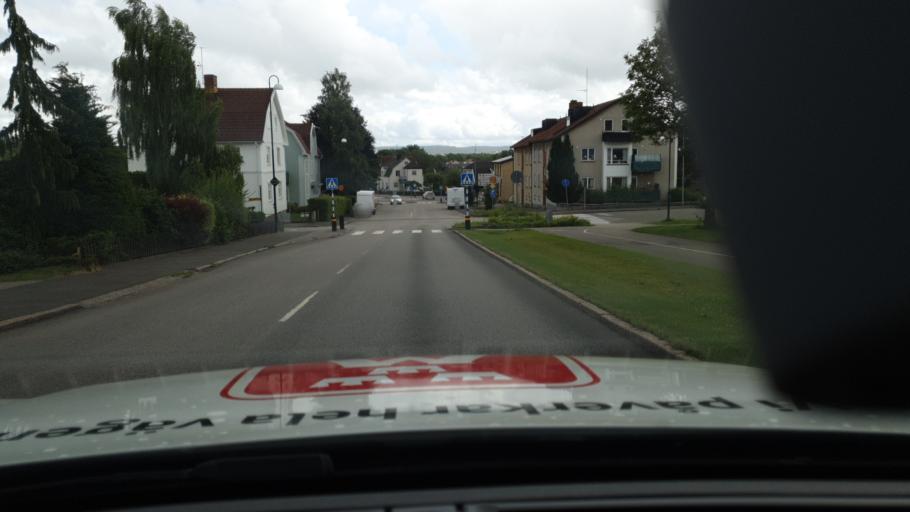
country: SE
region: Vaestra Goetaland
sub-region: Falkopings Kommun
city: Falkoeping
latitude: 58.1764
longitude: 13.5434
